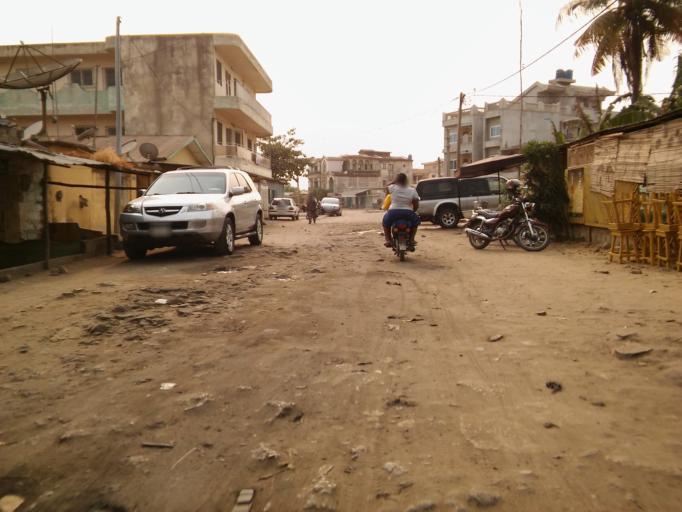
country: BJ
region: Littoral
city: Cotonou
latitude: 6.3595
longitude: 2.4018
